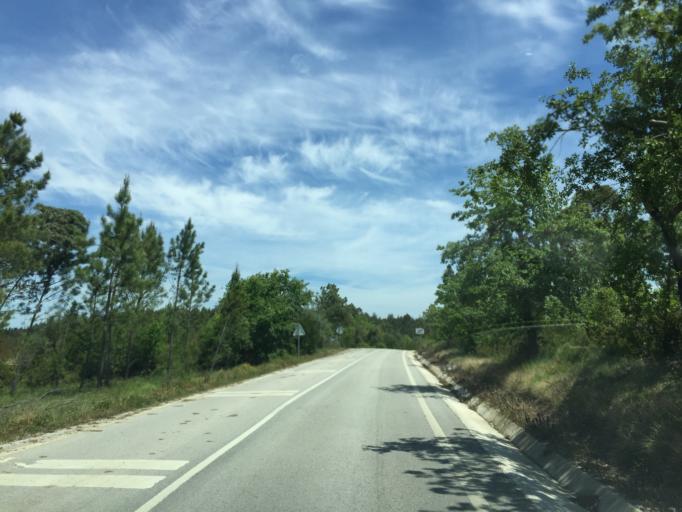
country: PT
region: Coimbra
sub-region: Soure
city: Soure
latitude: 40.0545
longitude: -8.6652
